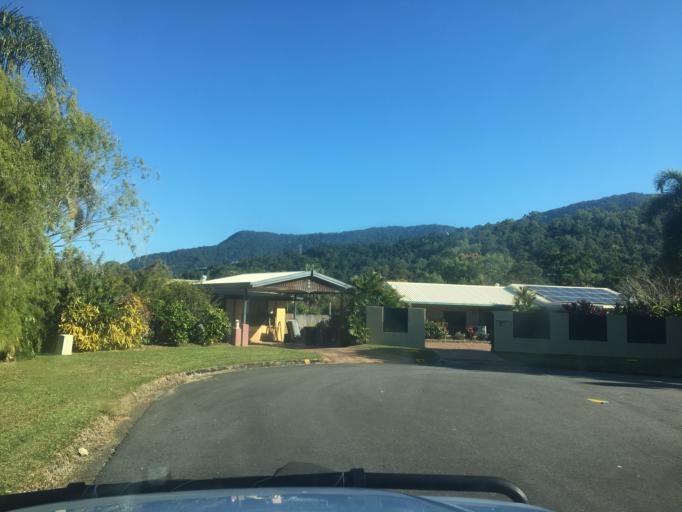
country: AU
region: Queensland
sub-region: Cairns
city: Woree
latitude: -16.9412
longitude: 145.7274
